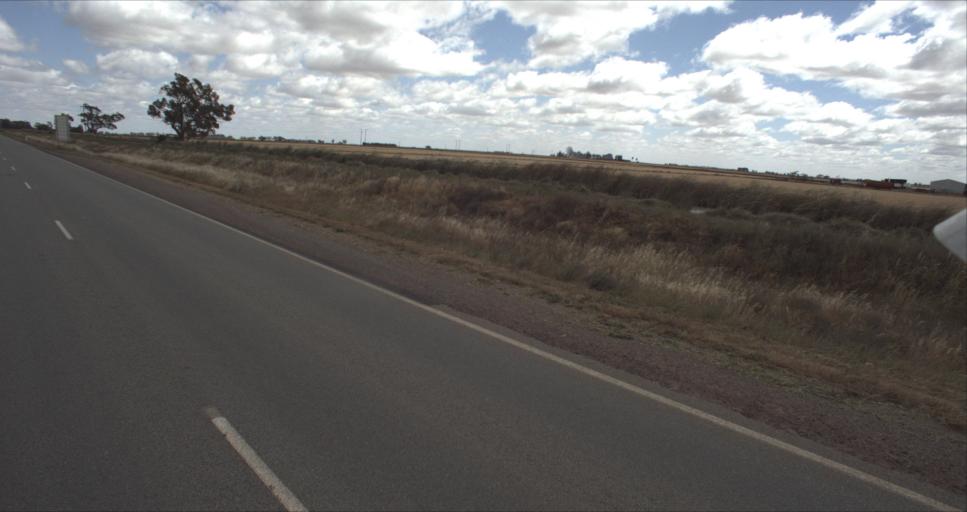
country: AU
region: New South Wales
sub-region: Murrumbidgee Shire
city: Darlington Point
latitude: -34.4969
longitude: 146.1867
